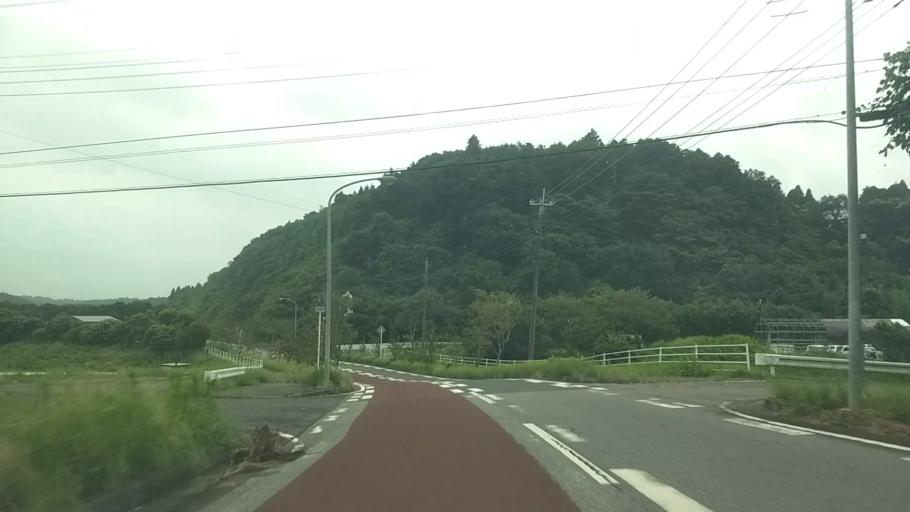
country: JP
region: Chiba
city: Kisarazu
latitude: 35.3799
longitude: 140.0075
